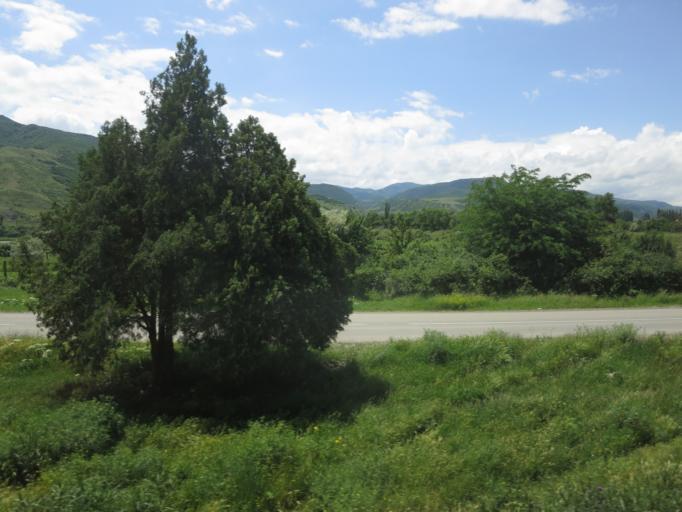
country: GE
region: Shida Kartli
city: Gori
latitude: 41.9956
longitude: 44.0247
